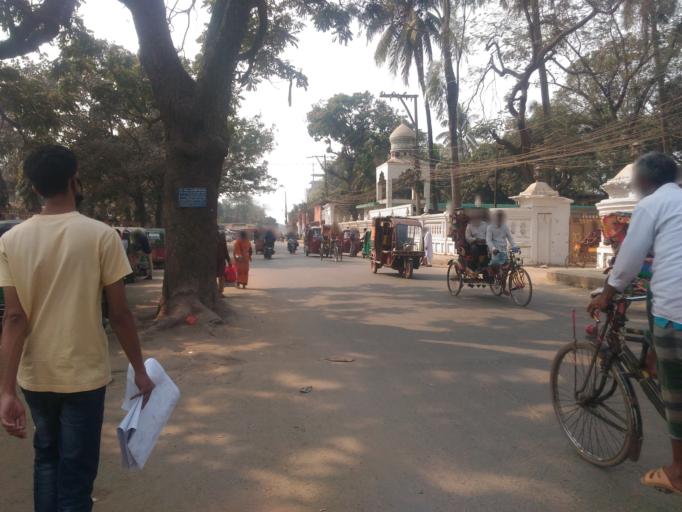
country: BD
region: Dhaka
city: Tungi
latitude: 24.0000
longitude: 90.4260
